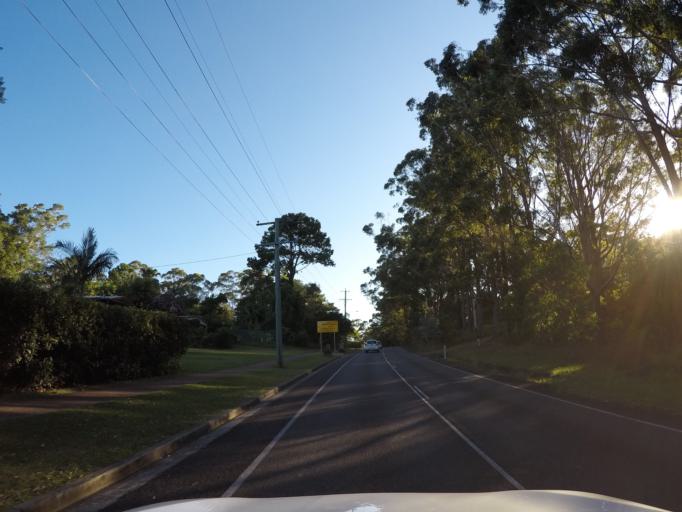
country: AU
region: Queensland
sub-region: Sunshine Coast
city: Nambour
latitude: -26.6298
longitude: 152.8593
